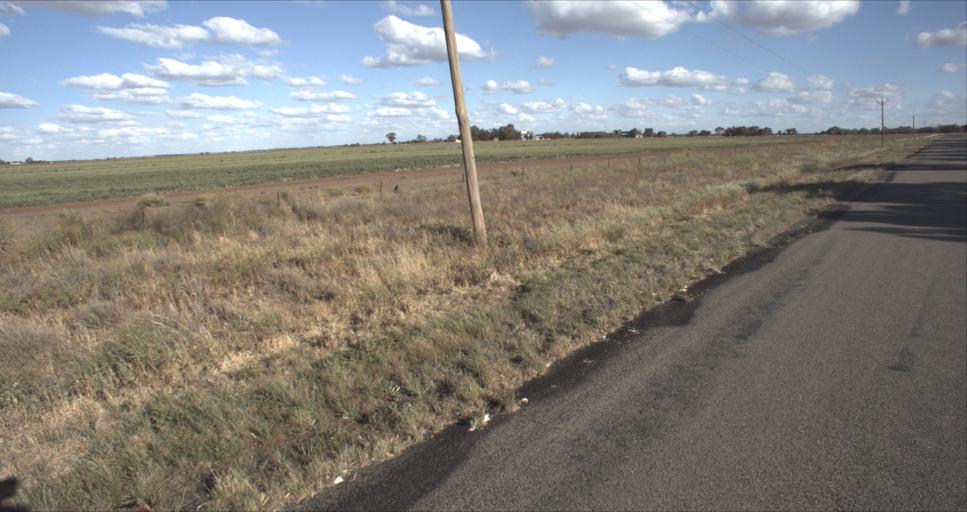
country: AU
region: New South Wales
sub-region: Leeton
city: Leeton
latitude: -34.5469
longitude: 146.2794
